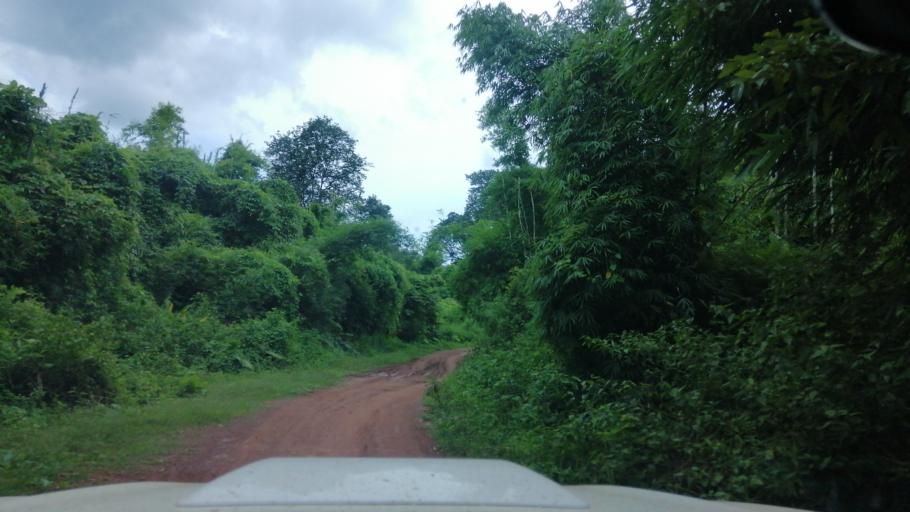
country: TH
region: Nan
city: Mae Charim
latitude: 18.7698
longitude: 101.3125
